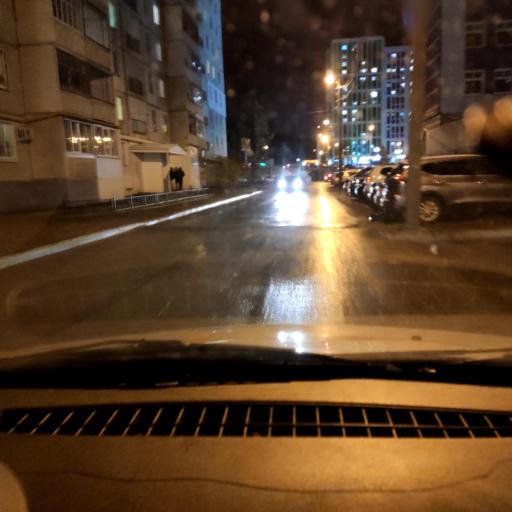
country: RU
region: Bashkortostan
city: Ufa
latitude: 54.7638
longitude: 56.0499
